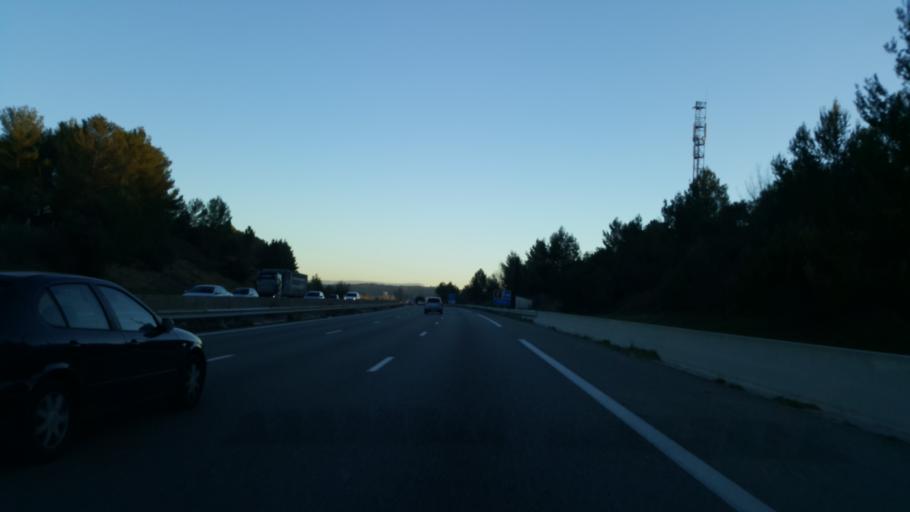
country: FR
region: Provence-Alpes-Cote d'Azur
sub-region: Departement des Bouches-du-Rhone
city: Meyreuil
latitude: 43.4904
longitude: 5.5277
